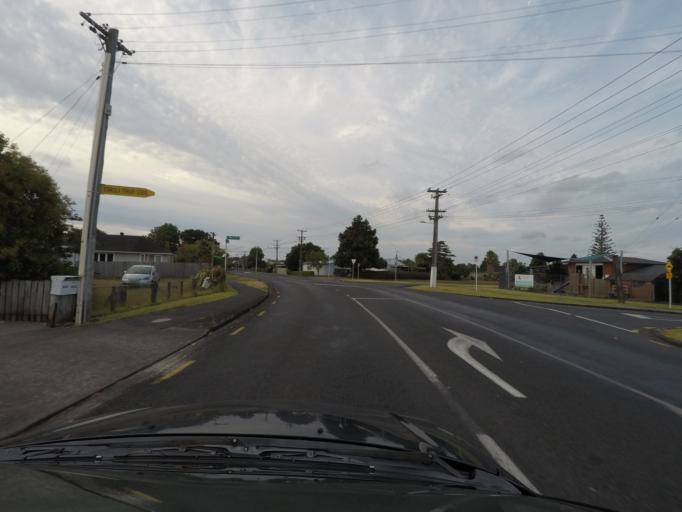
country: NZ
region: Auckland
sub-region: Auckland
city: Rosebank
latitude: -36.8341
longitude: 174.6495
